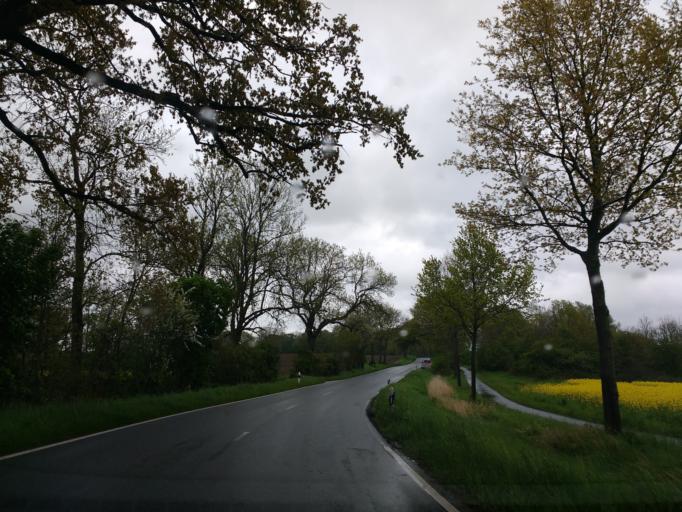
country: DE
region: Schleswig-Holstein
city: Waabs
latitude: 54.5178
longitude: 9.9402
